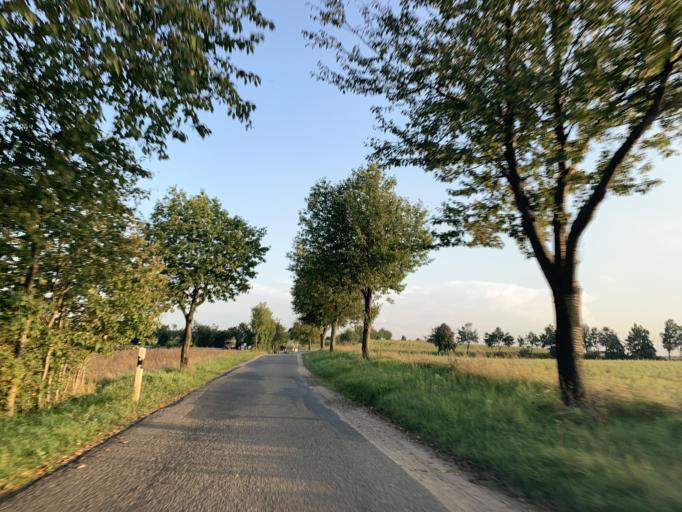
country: DE
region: Mecklenburg-Vorpommern
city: Loitz
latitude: 53.3657
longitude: 13.3851
